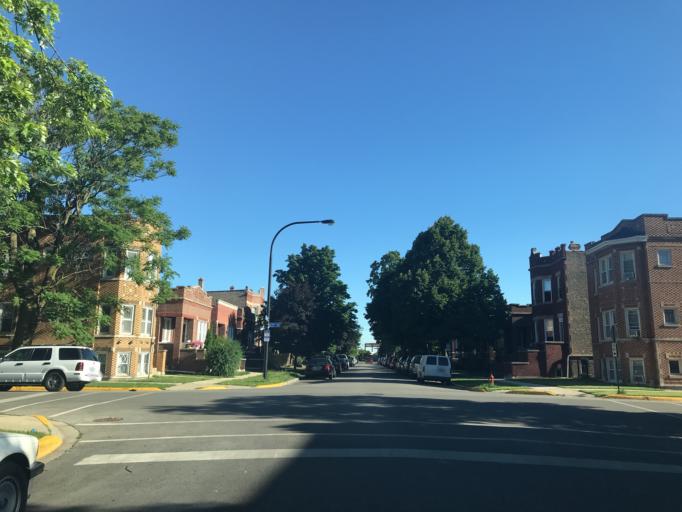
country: US
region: Illinois
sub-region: Cook County
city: Cicero
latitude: 41.8458
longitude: -87.7663
